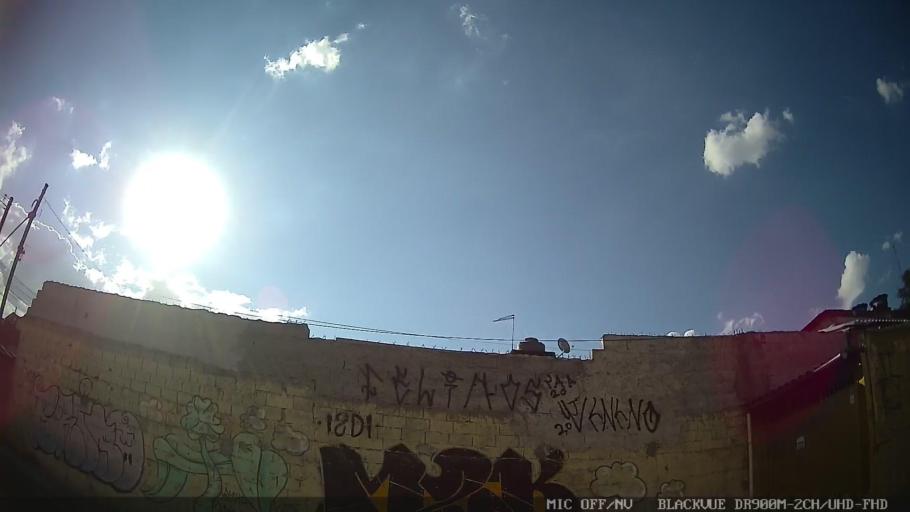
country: BR
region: Sao Paulo
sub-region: Ferraz De Vasconcelos
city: Ferraz de Vasconcelos
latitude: -23.5292
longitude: -46.4473
